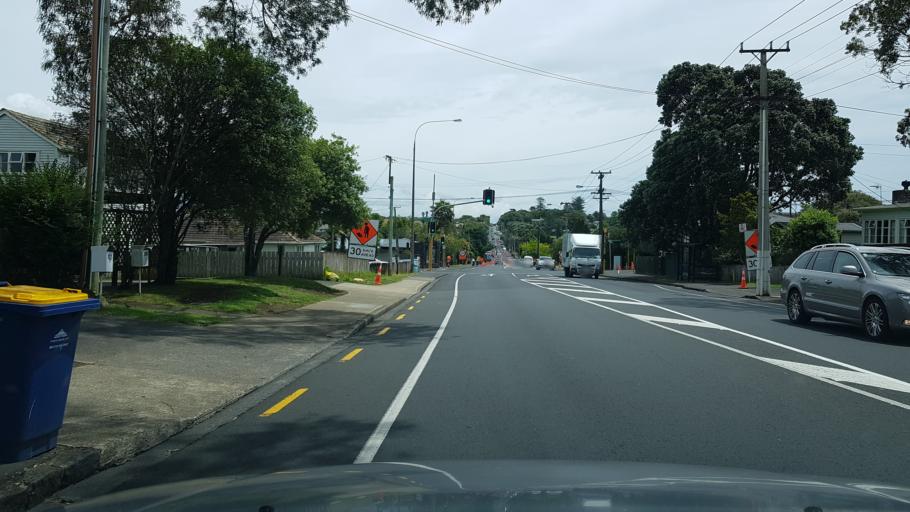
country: NZ
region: Auckland
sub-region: Auckland
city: North Shore
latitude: -36.8058
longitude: 174.7889
